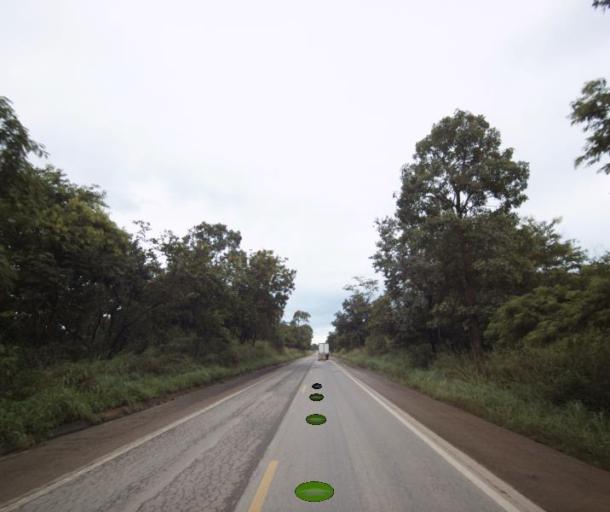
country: BR
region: Goias
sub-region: Porangatu
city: Porangatu
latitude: -13.6981
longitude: -49.0218
